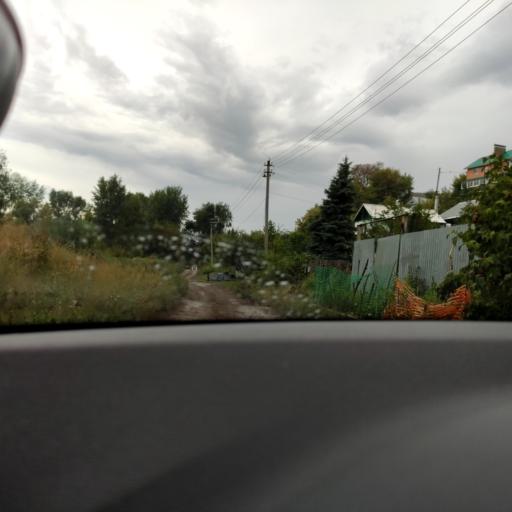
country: RU
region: Samara
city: Samara
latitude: 53.1713
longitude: 50.1605
